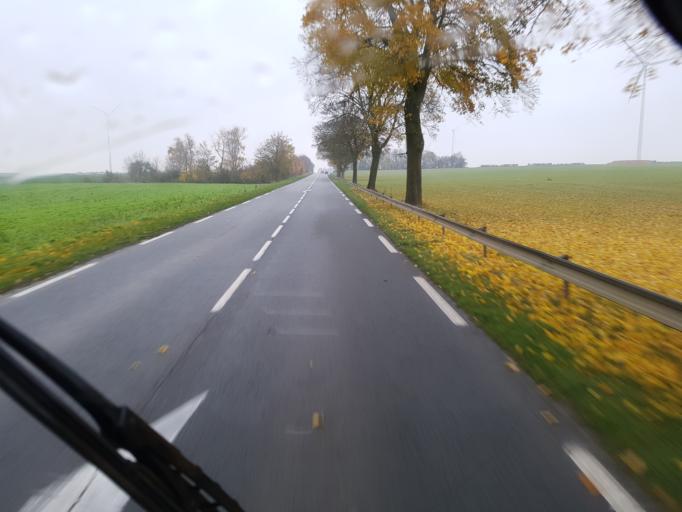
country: FR
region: Picardie
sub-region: Departement de l'Aisne
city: Omissy
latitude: 49.8953
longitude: 3.2636
